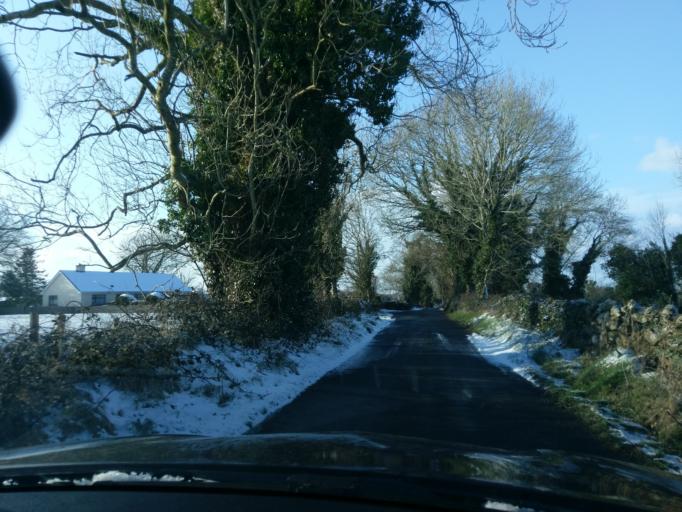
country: IE
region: Connaught
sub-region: County Galway
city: Athenry
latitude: 53.1950
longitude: -8.7350
